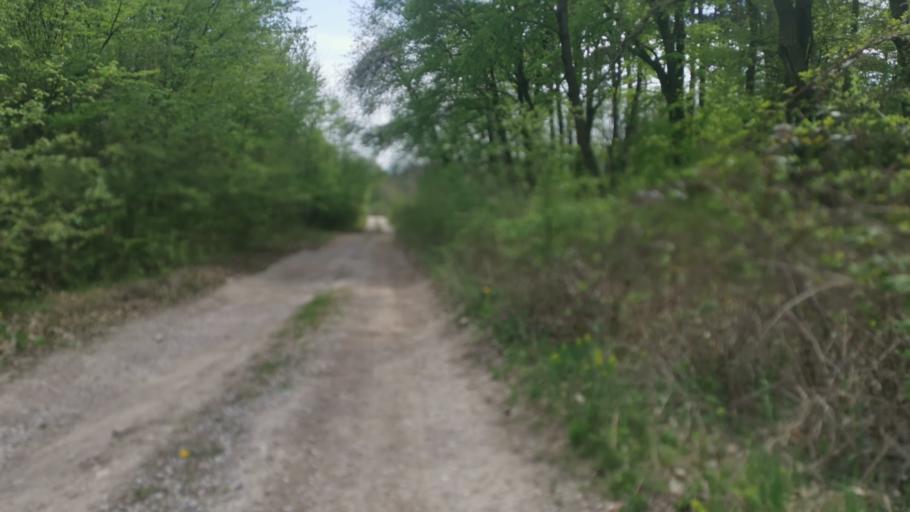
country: SK
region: Trnavsky
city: Smolenice
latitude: 48.5444
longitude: 17.4426
